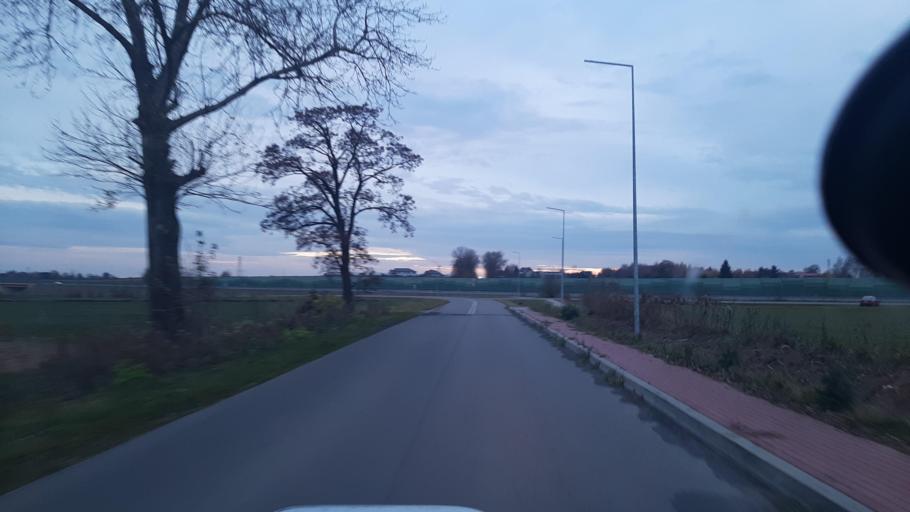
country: PL
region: Lublin Voivodeship
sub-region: Powiat lubelski
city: Garbow
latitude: 51.3522
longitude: 22.3684
